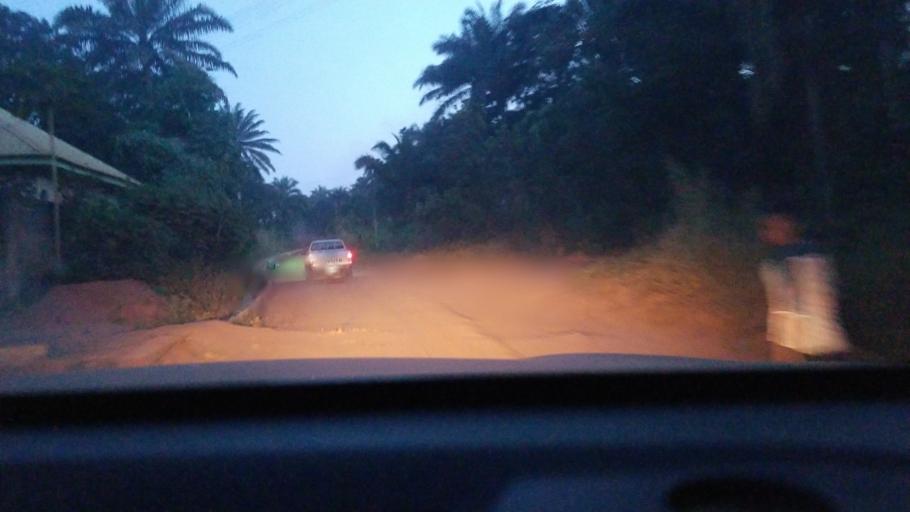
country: NG
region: Enugu
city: Obollo-Afor
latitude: 6.9039
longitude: 7.5096
